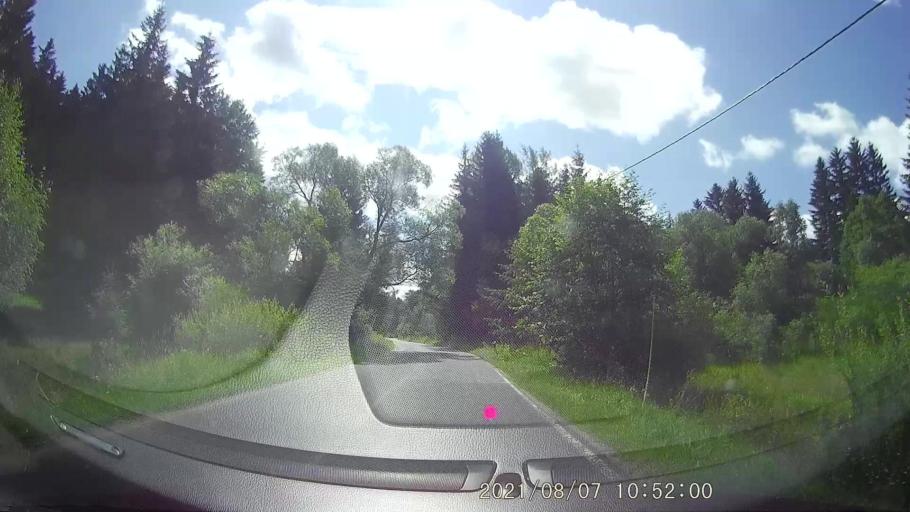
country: CZ
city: Rokytnice v Orlickych Horach
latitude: 50.2848
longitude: 16.4704
